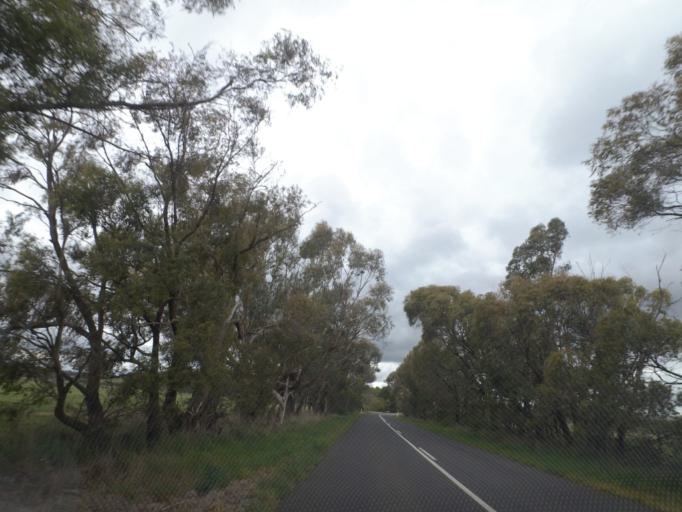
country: AU
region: Victoria
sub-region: Hume
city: Sunbury
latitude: -37.3623
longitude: 144.8252
